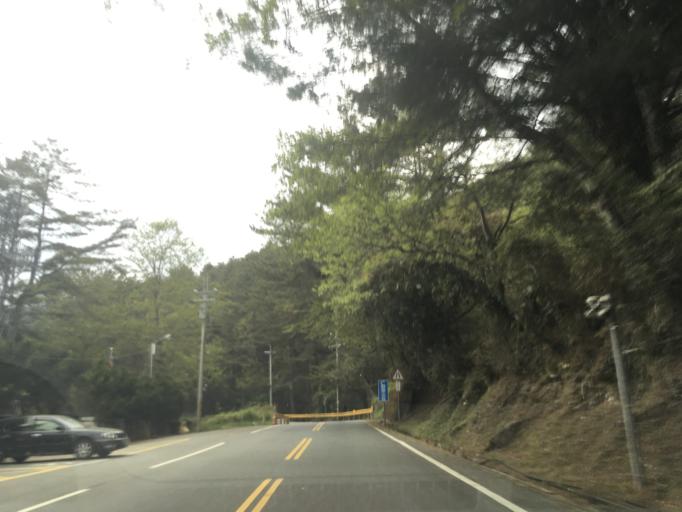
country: TW
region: Taiwan
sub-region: Hualien
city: Hualian
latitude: 24.1865
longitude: 121.3393
